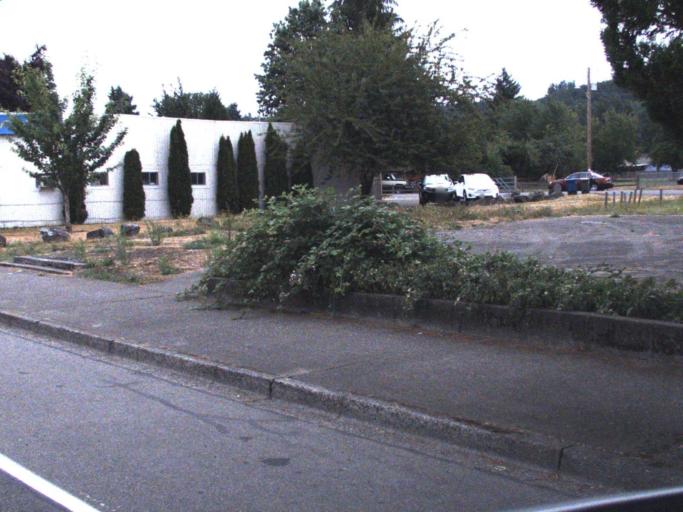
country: US
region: Washington
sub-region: King County
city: Carnation
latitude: 47.6473
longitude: -121.9147
